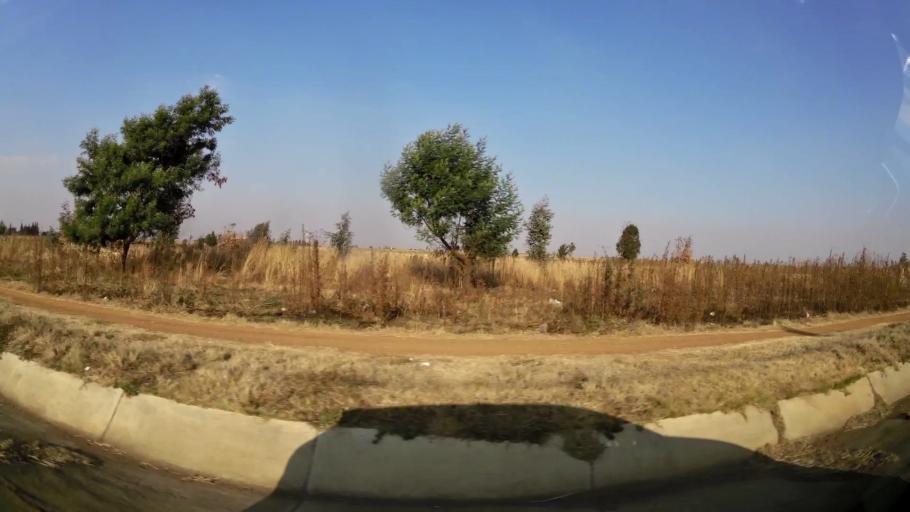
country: ZA
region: Gauteng
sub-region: Ekurhuleni Metropolitan Municipality
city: Benoni
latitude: -26.1412
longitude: 28.3896
